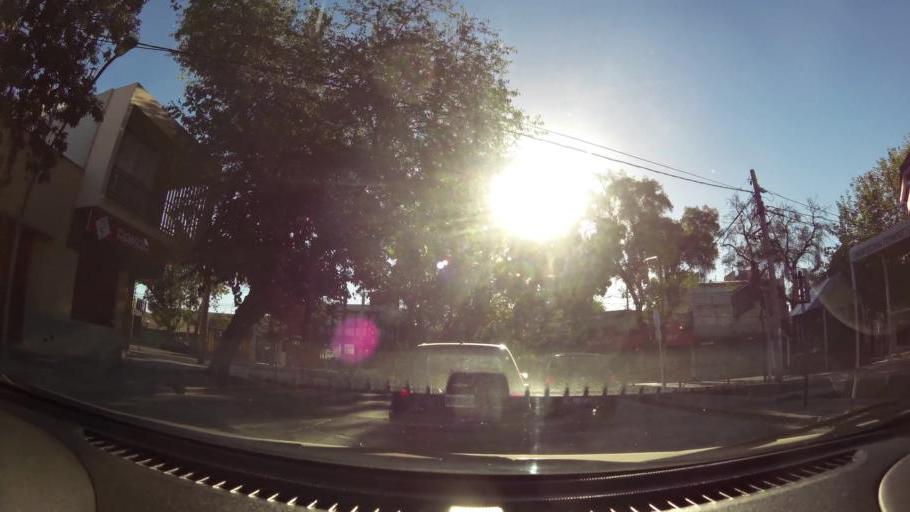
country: AR
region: Mendoza
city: Las Heras
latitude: -32.8667
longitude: -68.8329
